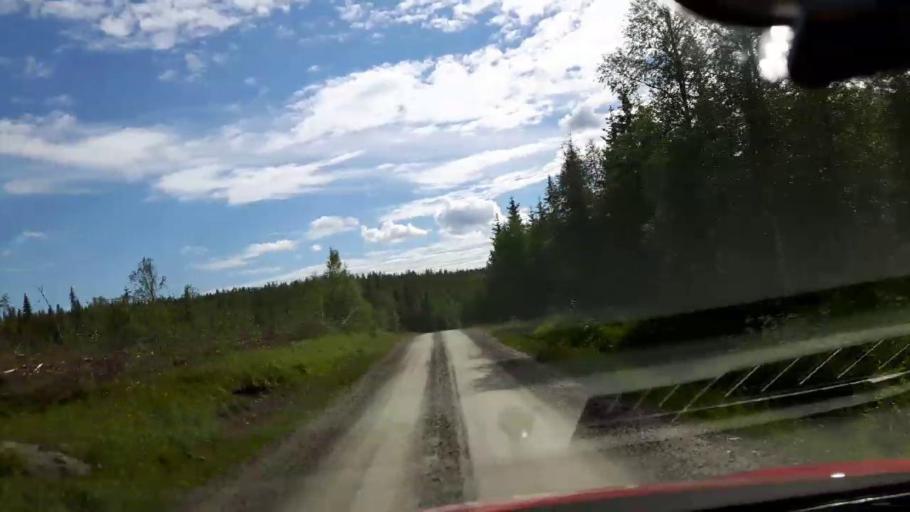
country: SE
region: Jaemtland
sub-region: Krokoms Kommun
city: Valla
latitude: 63.8954
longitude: 14.1739
